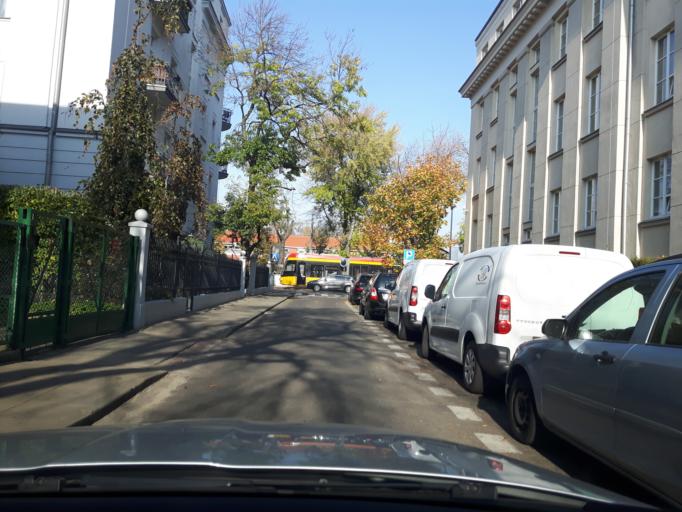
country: PL
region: Masovian Voivodeship
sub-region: Warszawa
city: Ochota
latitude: 52.2182
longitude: 20.9986
